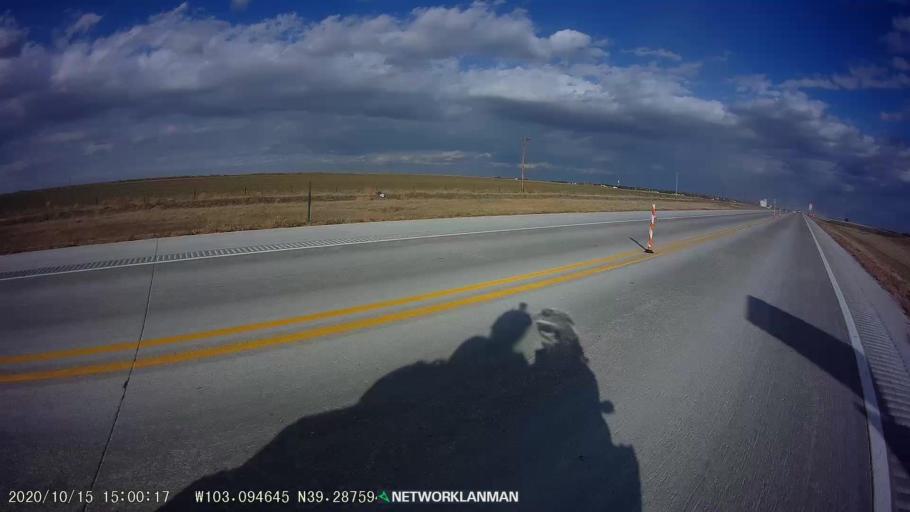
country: US
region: Colorado
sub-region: Lincoln County
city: Hugo
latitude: 39.2877
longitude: -103.0948
